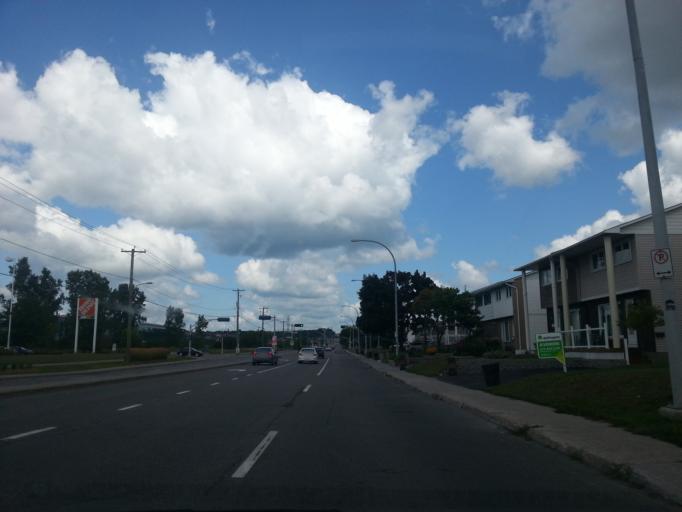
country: CA
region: Quebec
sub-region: Outaouais
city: Gatineau
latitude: 45.4842
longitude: -75.6743
